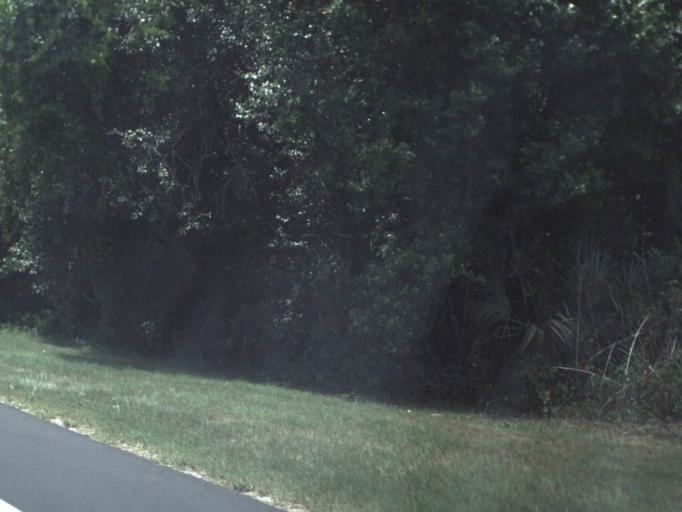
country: US
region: Florida
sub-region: Clay County
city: Keystone Heights
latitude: 29.7883
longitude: -82.0353
